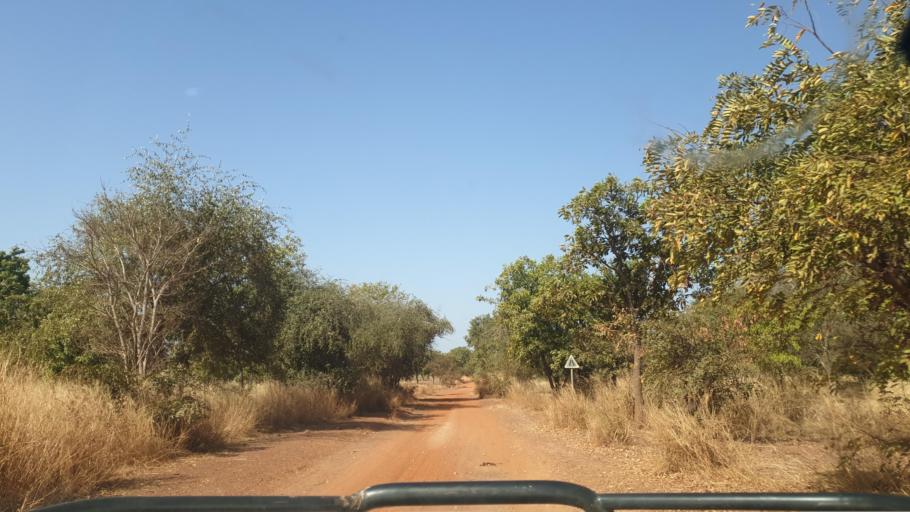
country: ML
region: Sikasso
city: Bougouni
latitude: 11.8215
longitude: -6.9684
